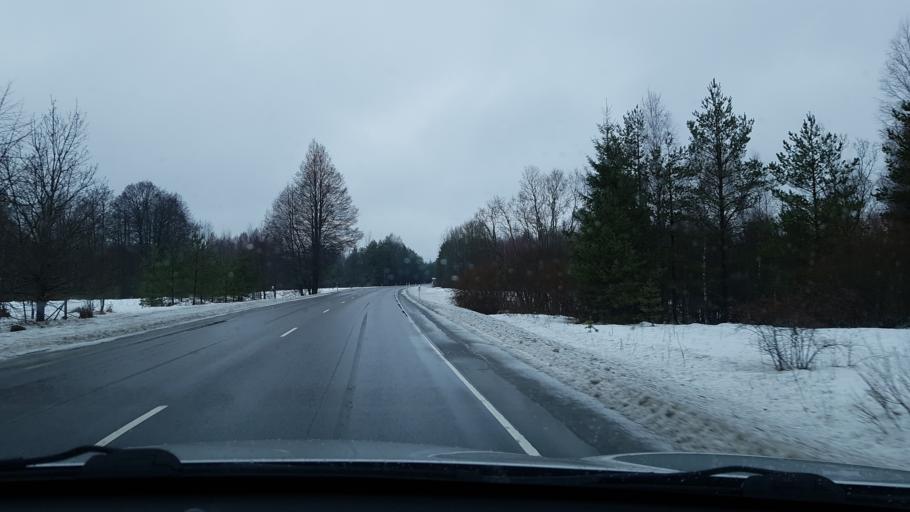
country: EE
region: Raplamaa
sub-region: Kehtna vald
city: Kehtna
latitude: 58.8694
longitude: 24.9876
